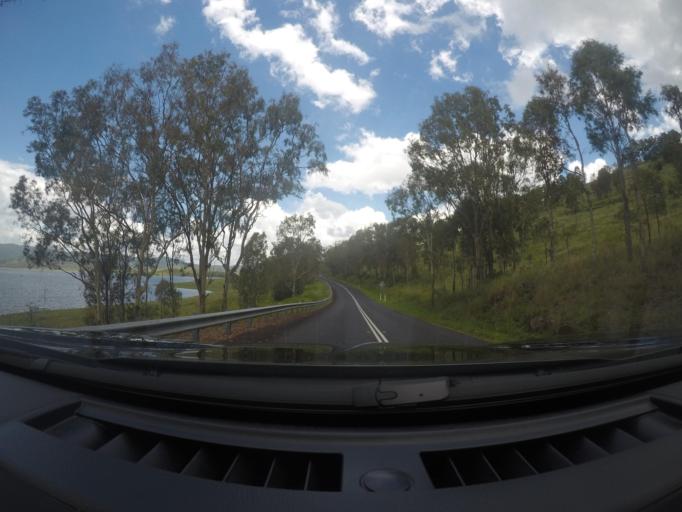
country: AU
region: Queensland
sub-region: Moreton Bay
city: Woodford
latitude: -27.0738
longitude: 152.5648
